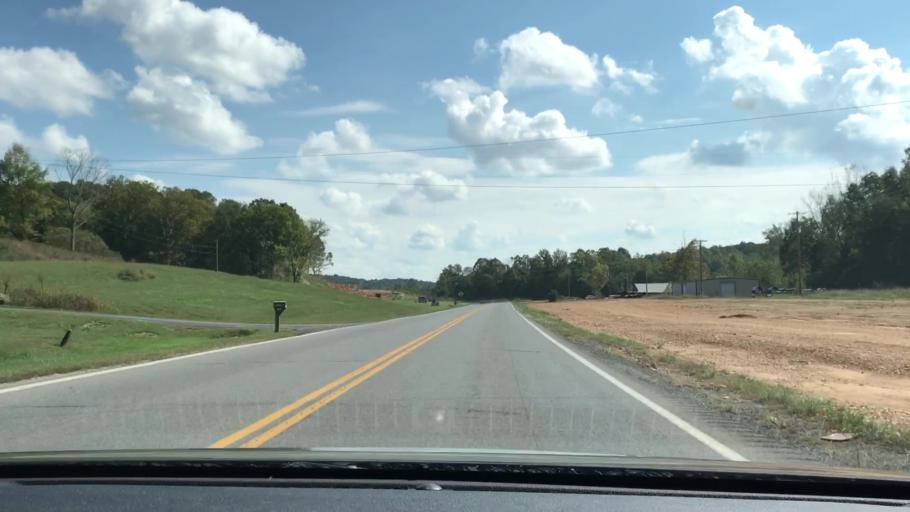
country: US
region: Kentucky
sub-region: Trigg County
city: Cadiz
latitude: 36.8054
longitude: -87.9233
